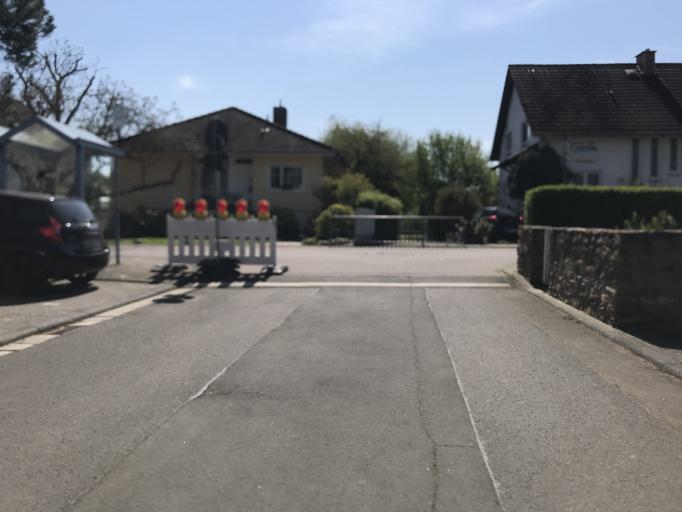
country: DE
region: Hesse
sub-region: Regierungsbezirk Darmstadt
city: Eltville
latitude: 50.0105
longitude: 8.1000
